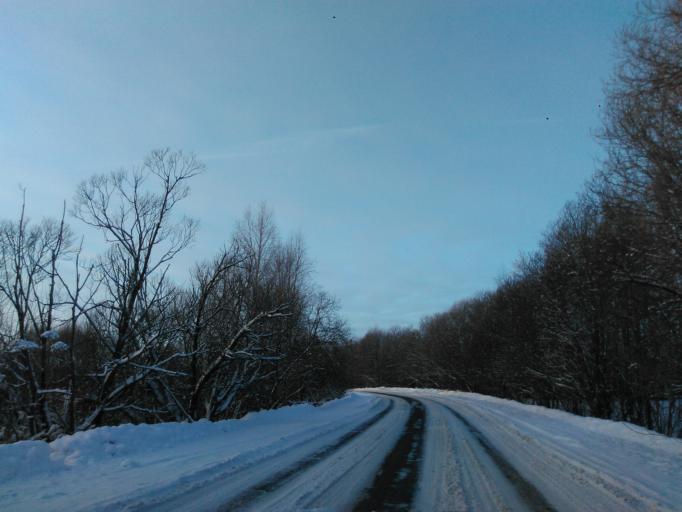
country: RU
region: Tverskaya
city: Zavidovo
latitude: 56.6348
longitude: 36.6225
